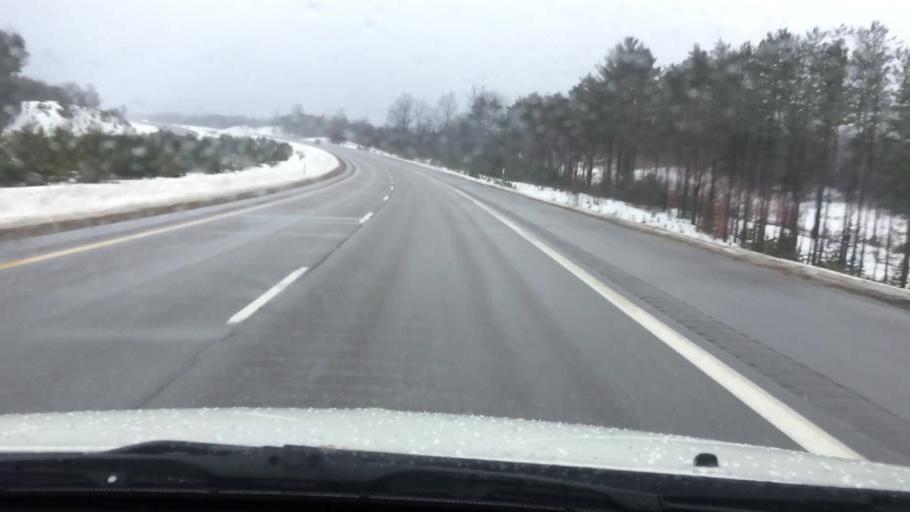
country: US
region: Michigan
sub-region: Wexford County
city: Manton
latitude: 44.3700
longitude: -85.4008
